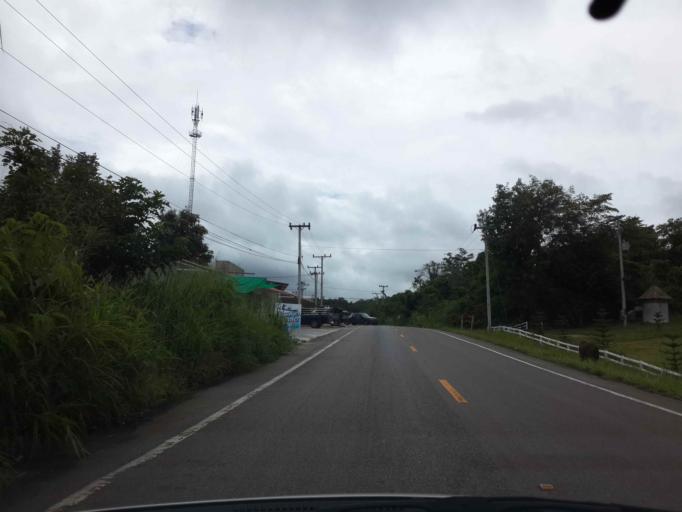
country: TH
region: Ratchaburi
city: Suan Phueng
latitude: 13.7024
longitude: 99.1985
